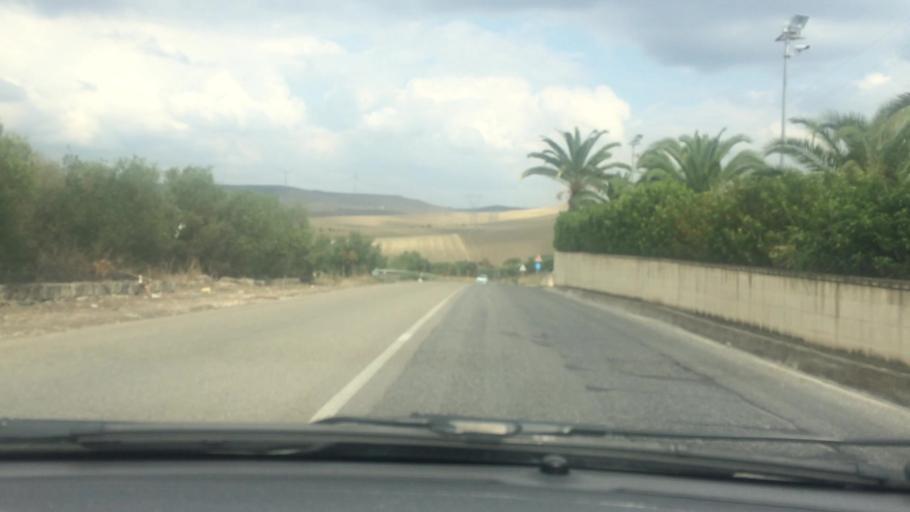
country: IT
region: Basilicate
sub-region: Provincia di Matera
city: Matera
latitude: 40.6865
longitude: 16.5698
